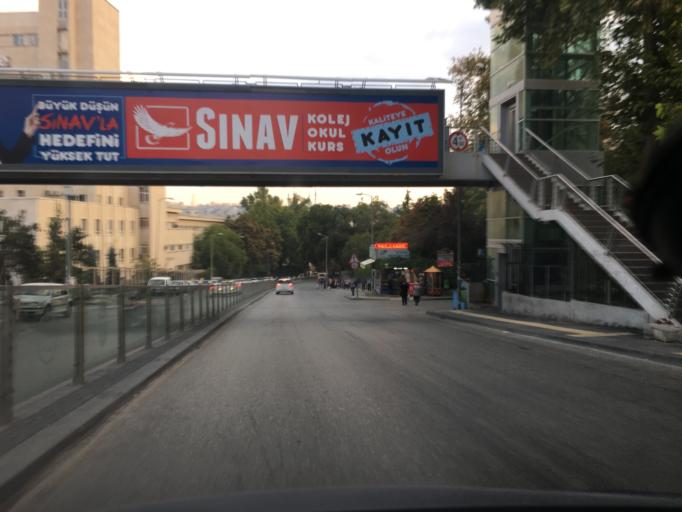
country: TR
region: Ankara
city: Ankara
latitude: 39.9315
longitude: 32.8600
